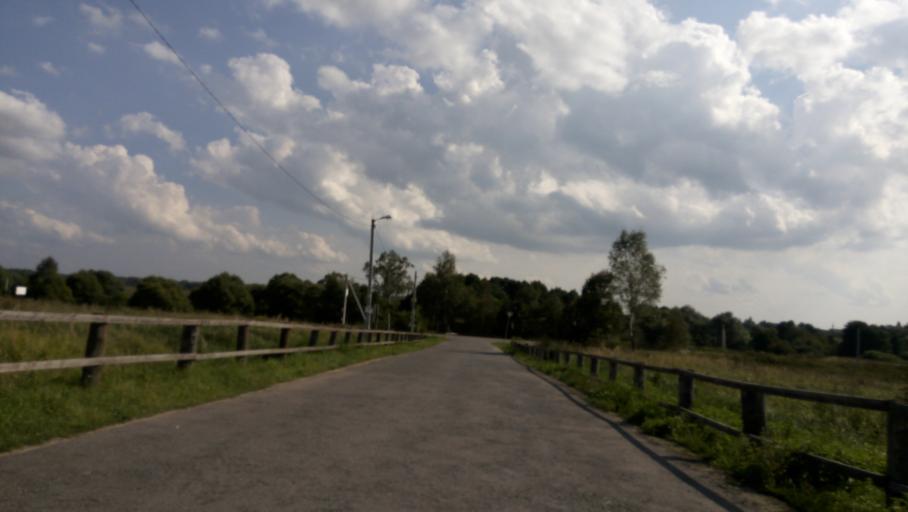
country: RU
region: Moskovskaya
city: Proletarskiy
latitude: 55.0419
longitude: 37.4137
